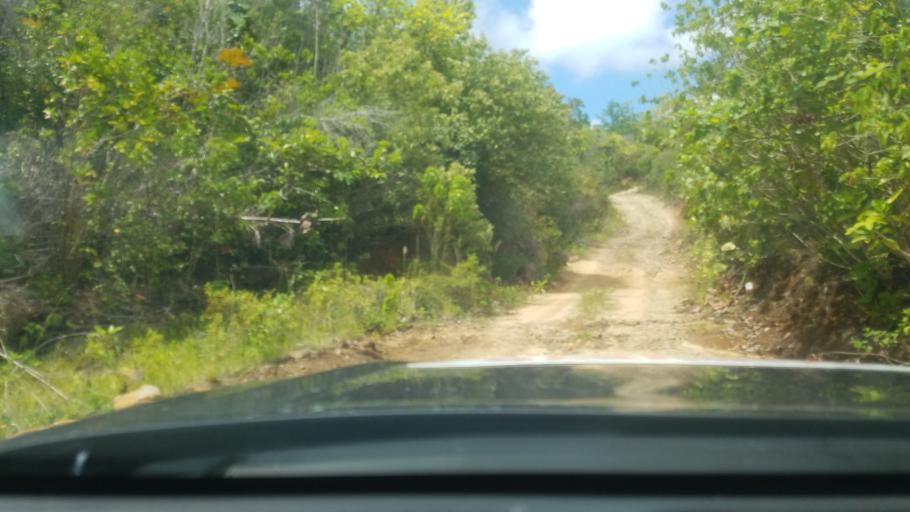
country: LC
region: Praslin
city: Praslin
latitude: 13.8688
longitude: -60.8934
